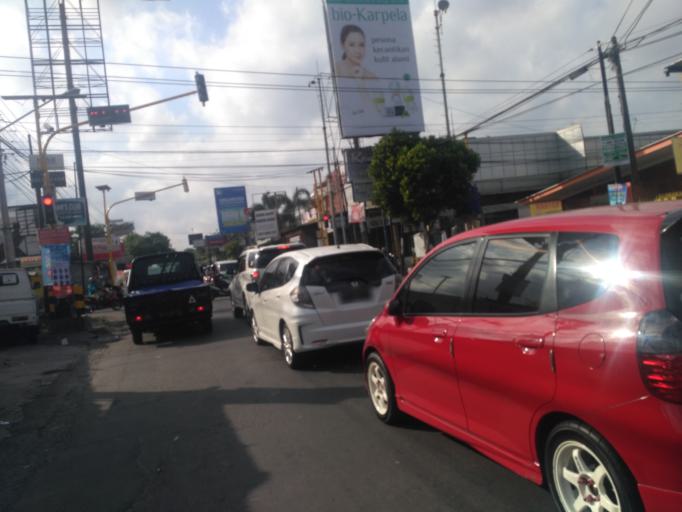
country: ID
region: Daerah Istimewa Yogyakarta
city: Yogyakarta
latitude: -7.7791
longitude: 110.3407
